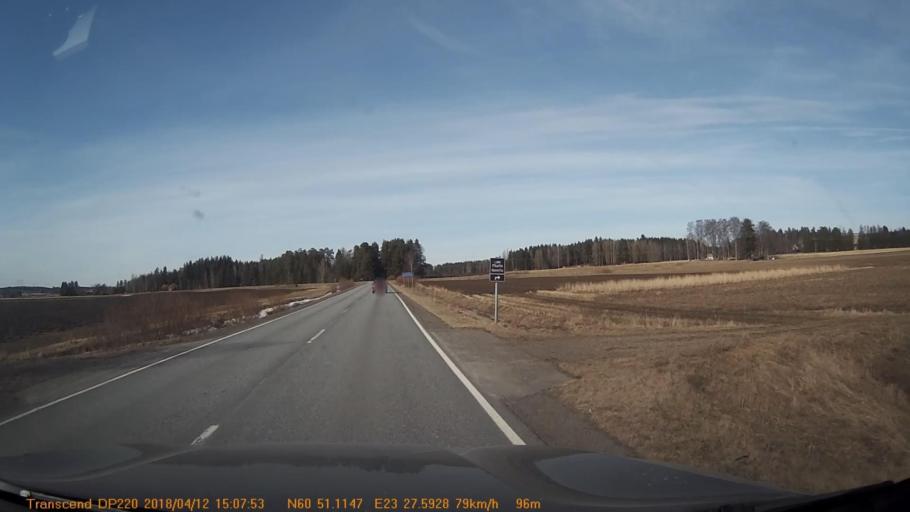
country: FI
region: Haeme
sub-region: Forssa
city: Jokioinen
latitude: 60.8524
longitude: 23.4598
